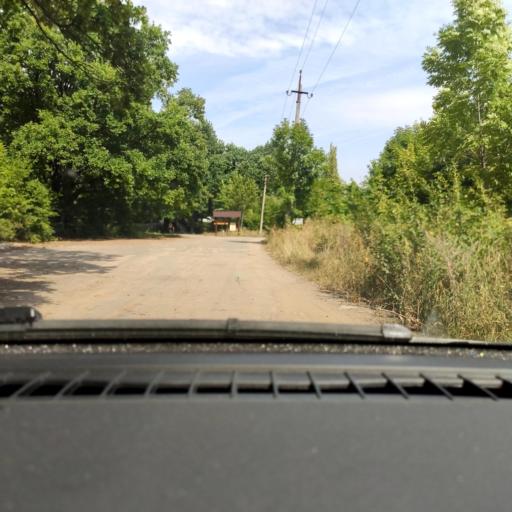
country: RU
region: Voronezj
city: Pridonskoy
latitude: 51.7564
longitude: 39.0793
